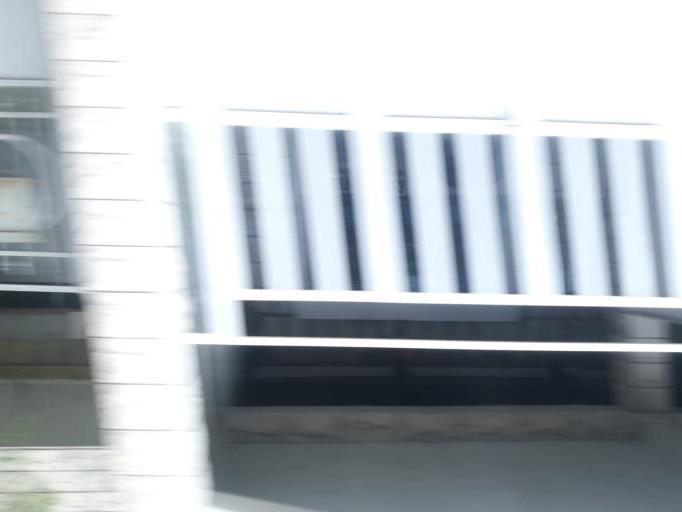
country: HR
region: Splitsko-Dalmatinska
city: Jesenice
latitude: 43.4618
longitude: 16.5993
